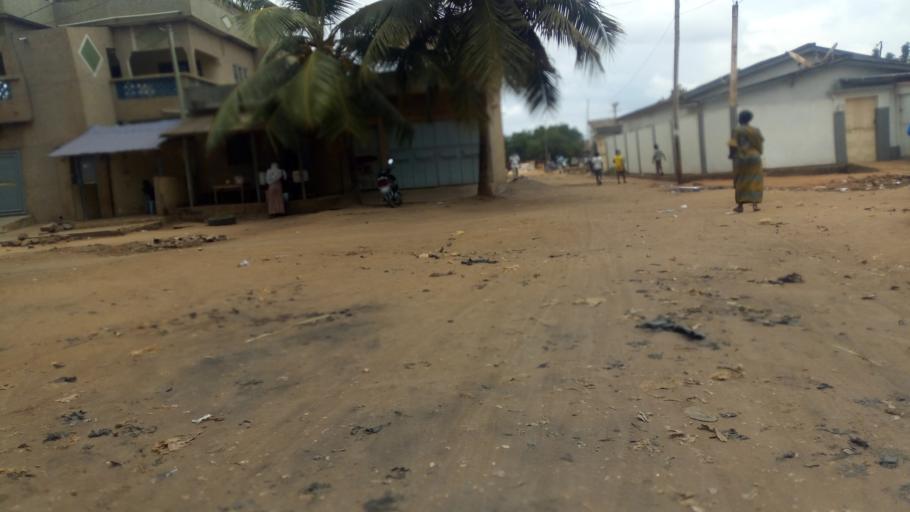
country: TG
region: Maritime
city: Lome
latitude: 6.2338
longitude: 1.1829
